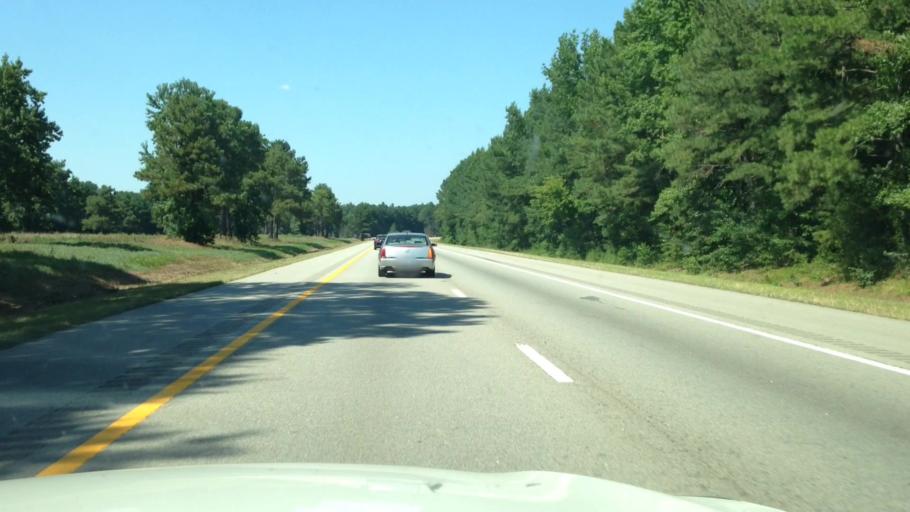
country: US
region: North Carolina
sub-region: Johnston County
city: Kenly
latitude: 35.6536
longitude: -78.0948
